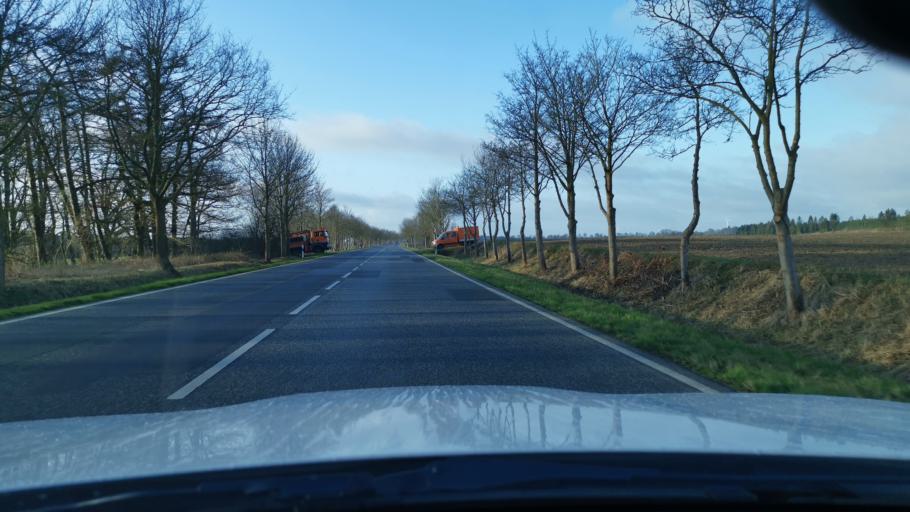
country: DE
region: Mecklenburg-Vorpommern
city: Laage
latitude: 53.9123
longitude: 12.3172
